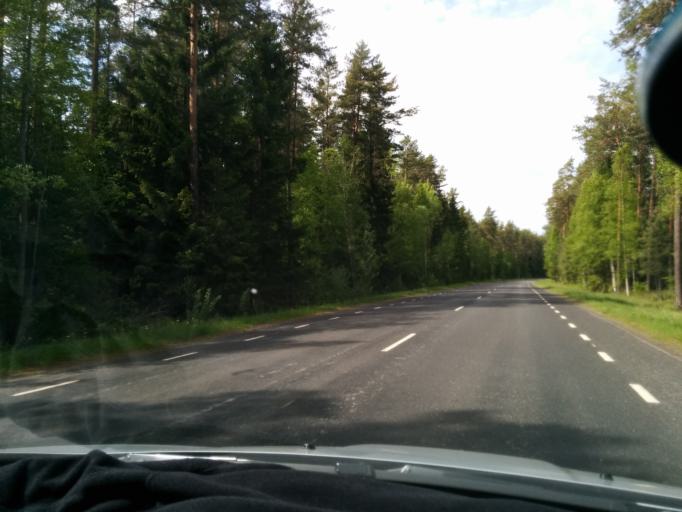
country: EE
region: Harju
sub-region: Loksa linn
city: Loksa
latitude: 59.5536
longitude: 25.7297
